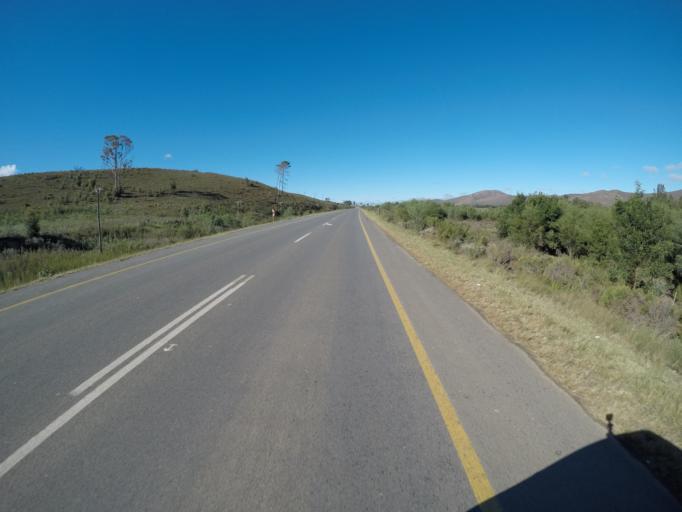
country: ZA
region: Western Cape
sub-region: Overberg District Municipality
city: Caledon
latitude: -34.0506
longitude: 19.5870
